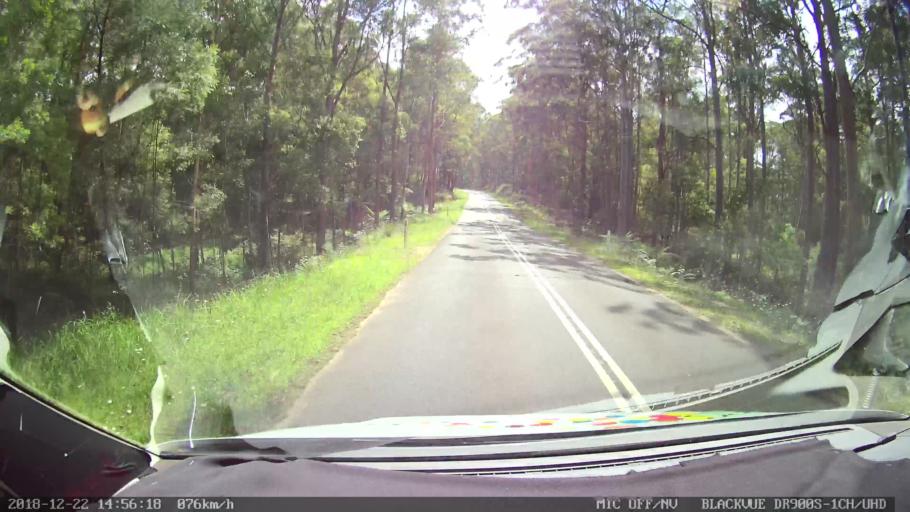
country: AU
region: New South Wales
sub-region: Bellingen
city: Dorrigo
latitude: -30.2324
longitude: 152.5143
